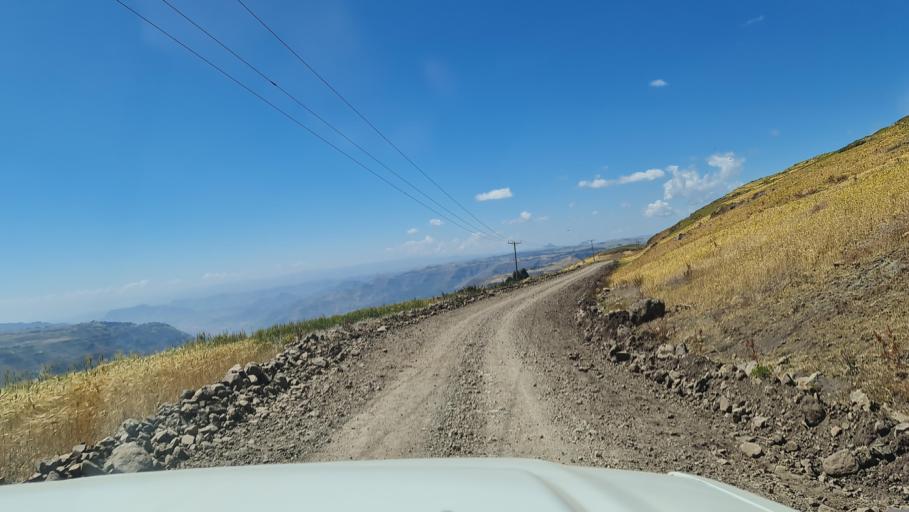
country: ET
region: Amhara
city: Debark'
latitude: 13.2312
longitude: 38.1016
